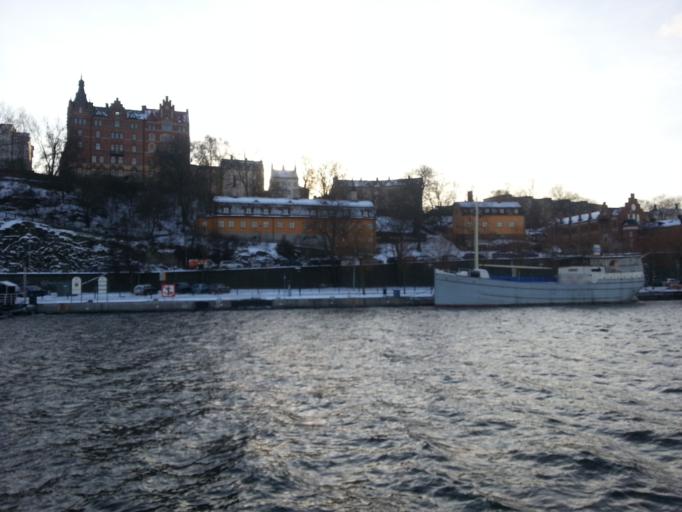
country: SE
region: Stockholm
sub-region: Stockholms Kommun
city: Stockholm
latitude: 59.3220
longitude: 18.0583
